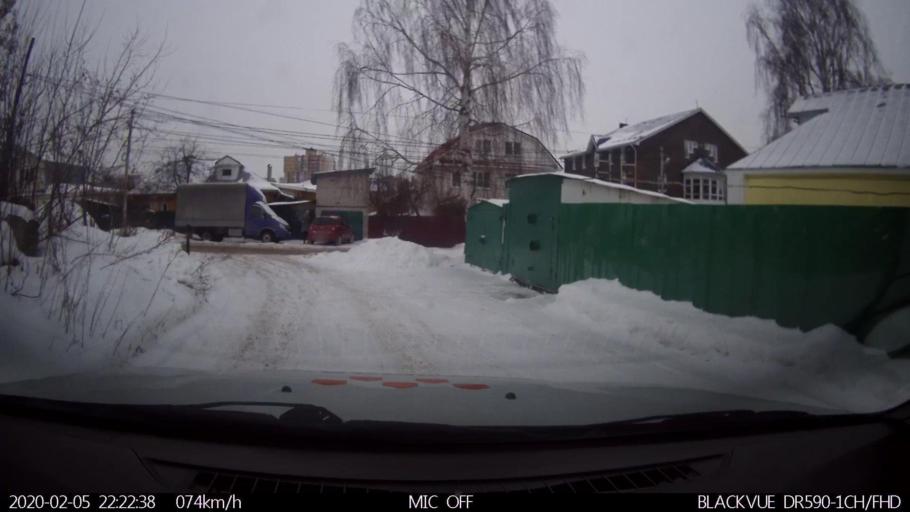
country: RU
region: Nizjnij Novgorod
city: Pervomaysk
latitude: 54.7649
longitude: 44.0156
